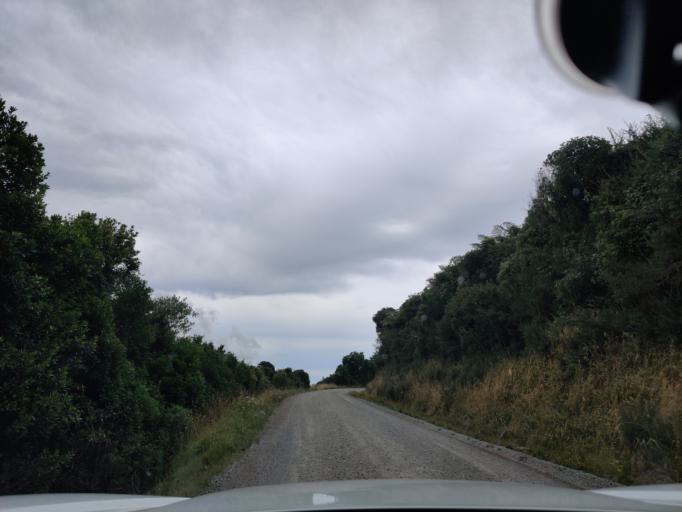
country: NZ
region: Wellington
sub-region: Masterton District
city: Masterton
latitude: -41.0383
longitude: 175.4152
